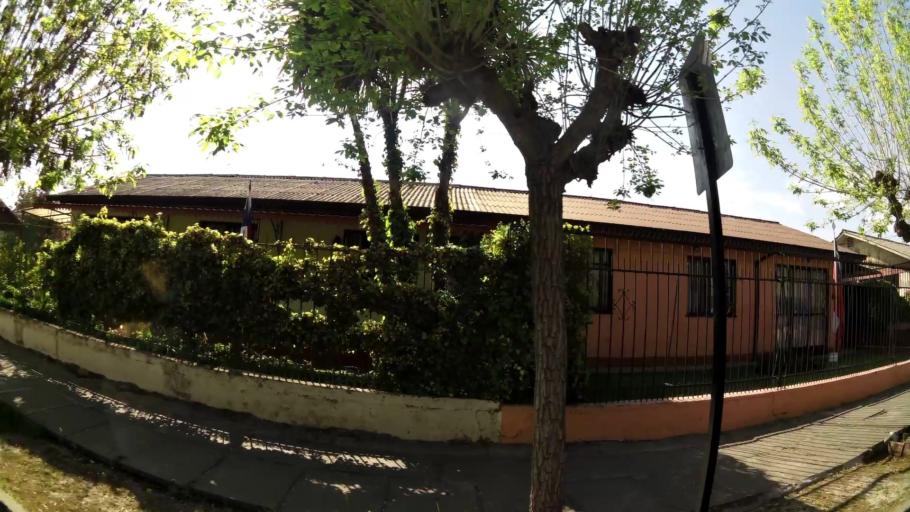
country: CL
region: Santiago Metropolitan
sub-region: Provincia de Santiago
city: La Pintana
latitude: -33.5570
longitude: -70.5906
